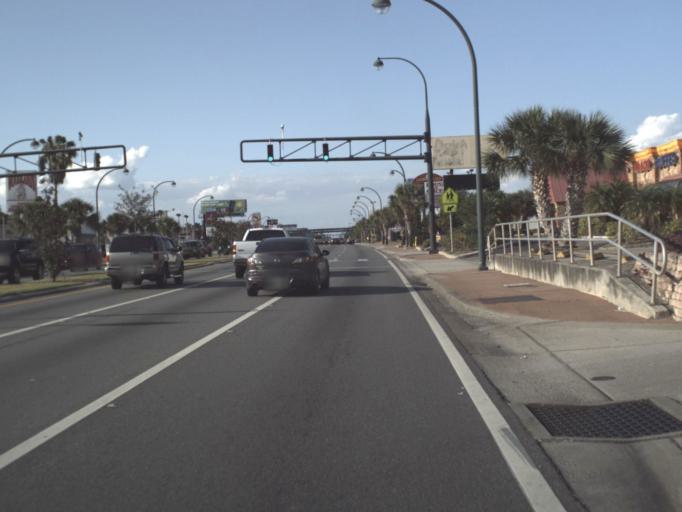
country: US
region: Florida
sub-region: Orange County
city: Sky Lake
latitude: 28.4679
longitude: -81.3965
